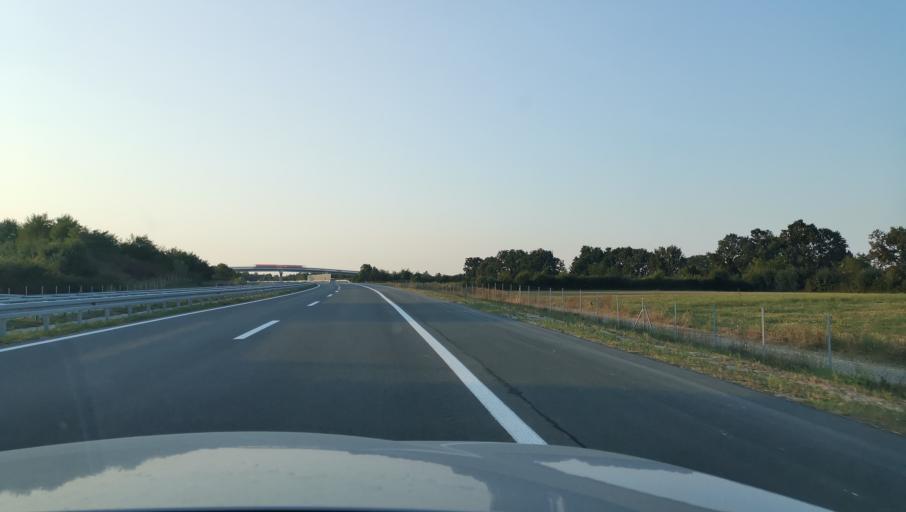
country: RS
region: Central Serbia
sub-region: Kolubarski Okrug
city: Lajkovac
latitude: 44.3753
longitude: 20.1178
